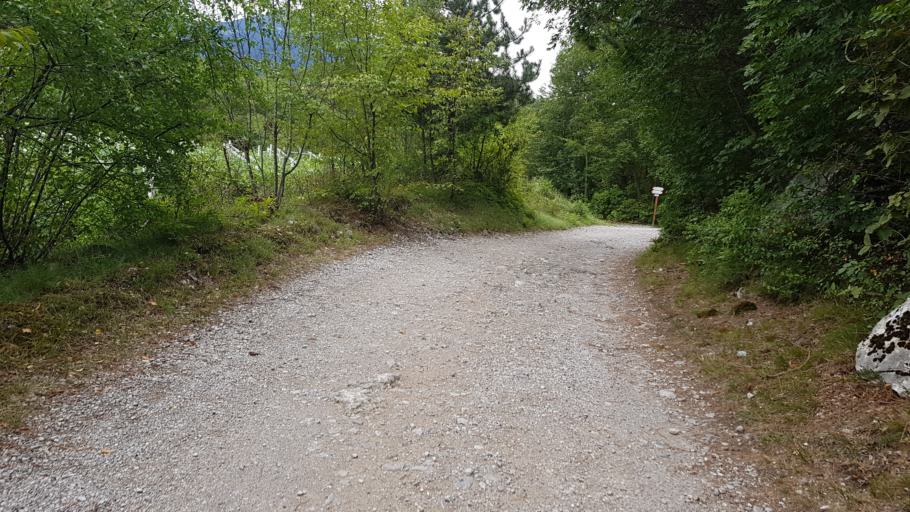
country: IT
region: Trentino-Alto Adige
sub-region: Provincia di Trento
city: Cavedine
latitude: 46.0046
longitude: 10.9709
